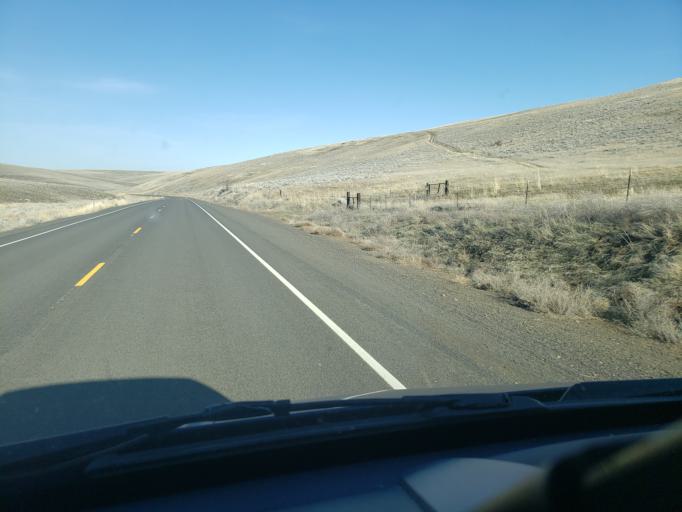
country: US
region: Oregon
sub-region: Umatilla County
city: Pilot Rock
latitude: 45.4596
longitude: -118.9349
